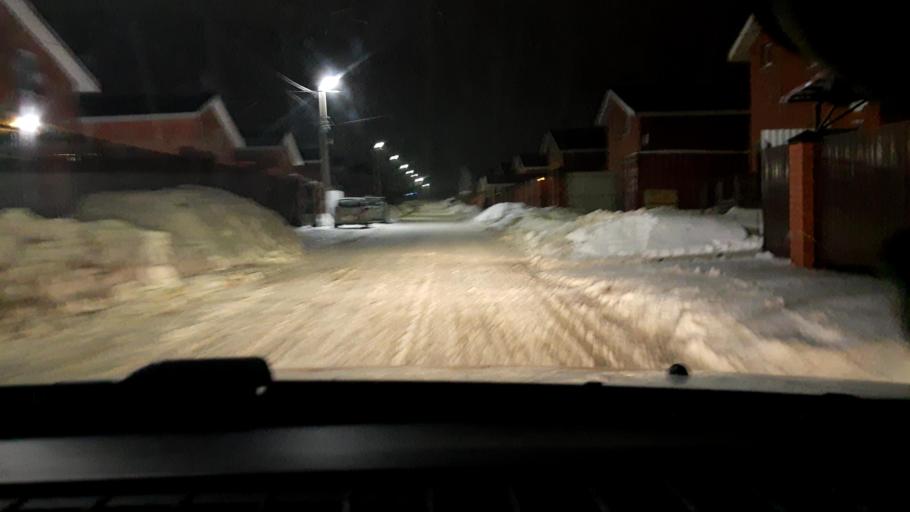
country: RU
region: Nizjnij Novgorod
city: Afonino
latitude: 56.1982
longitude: 44.0794
